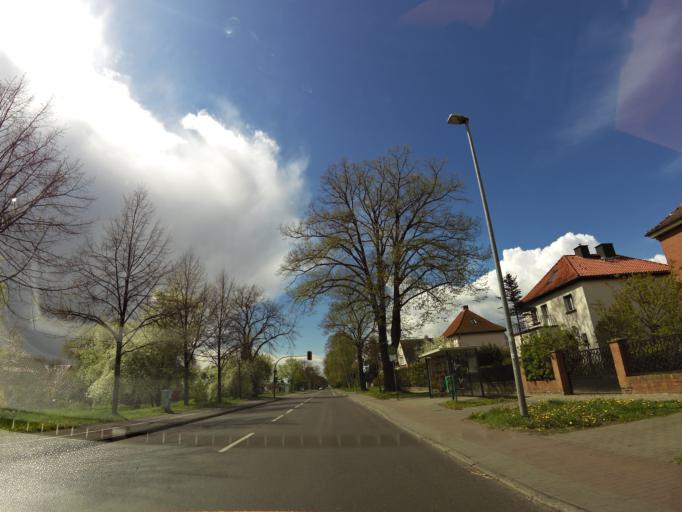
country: DE
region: Saxony-Anhalt
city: Diesdorf
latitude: 52.1028
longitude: 11.5845
